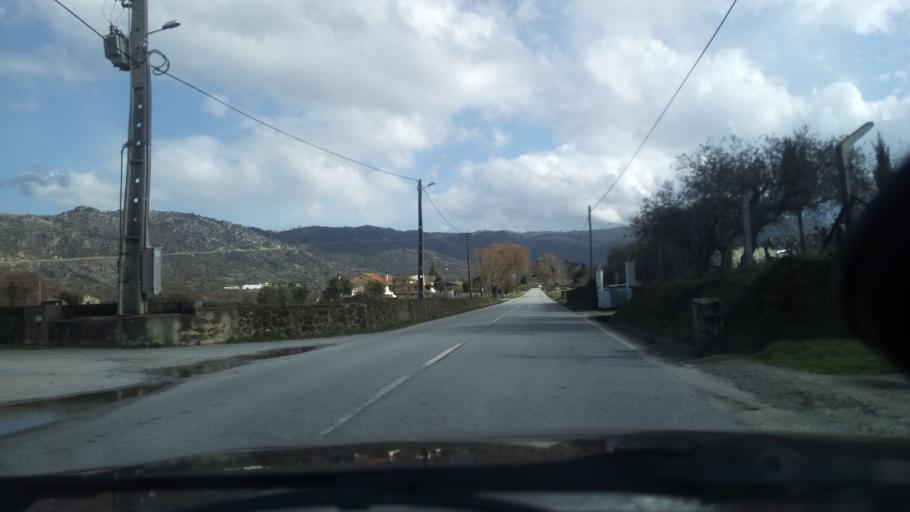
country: PT
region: Guarda
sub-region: Celorico da Beira
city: Celorico da Beira
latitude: 40.6158
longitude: -7.3077
